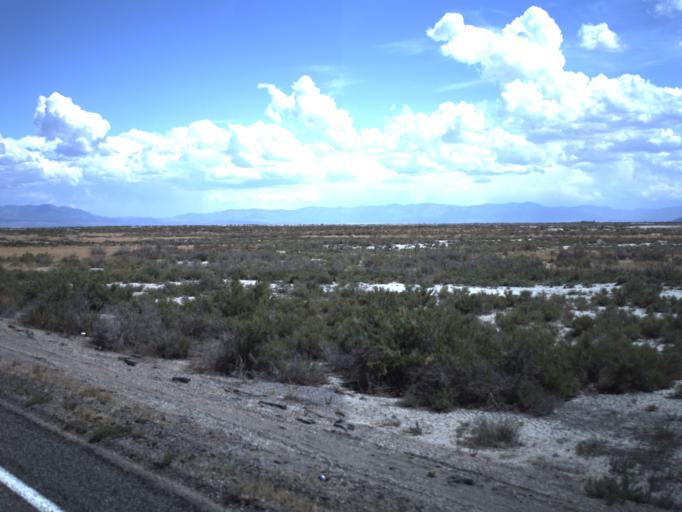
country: US
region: Utah
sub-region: Millard County
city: Delta
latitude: 39.3087
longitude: -112.7838
